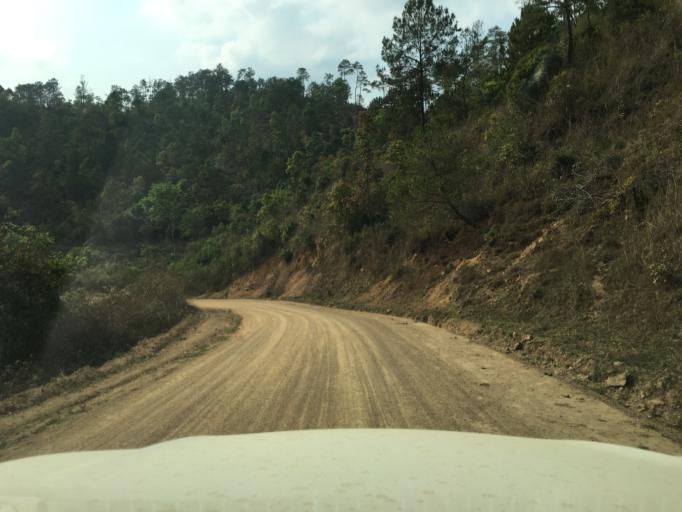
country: LA
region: Houaphan
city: Huameung
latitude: 20.2111
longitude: 103.8649
